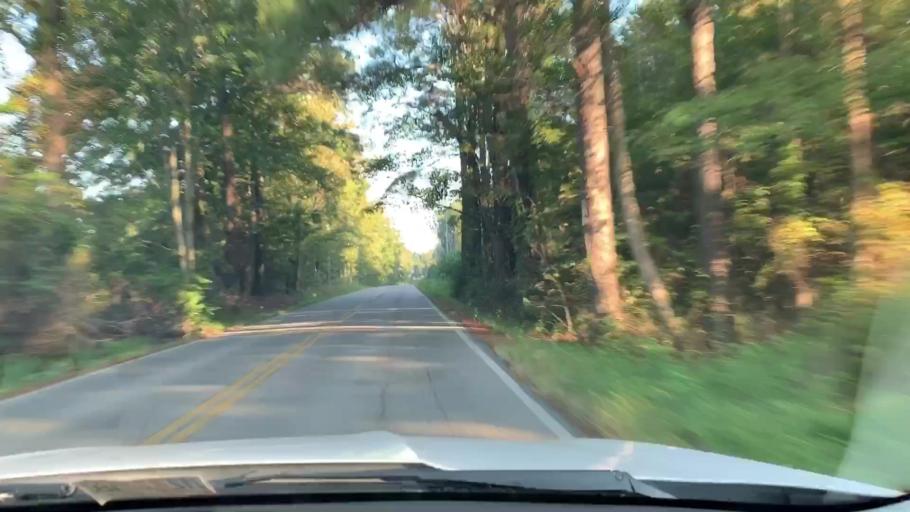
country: US
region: Virginia
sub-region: Middlesex County
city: Deltaville
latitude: 37.5626
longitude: -76.4511
